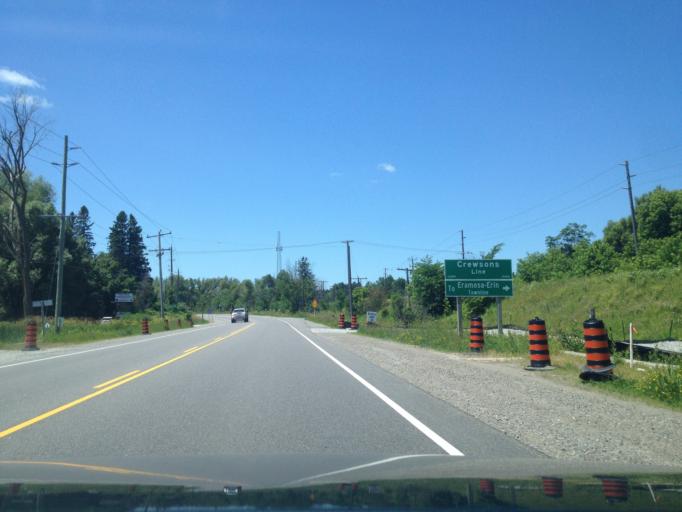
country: CA
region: Ontario
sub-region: Wellington County
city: Guelph
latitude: 43.6286
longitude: -80.0832
